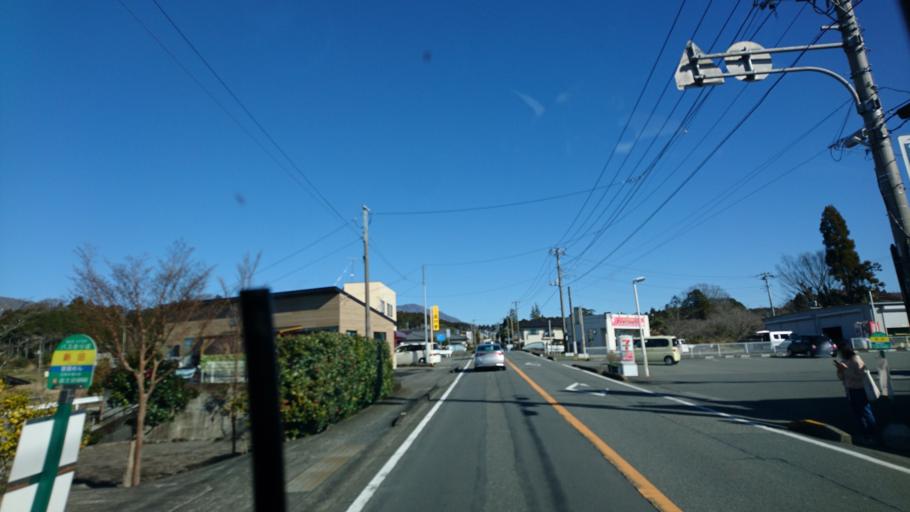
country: JP
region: Shizuoka
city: Fujinomiya
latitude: 35.3051
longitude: 138.5941
